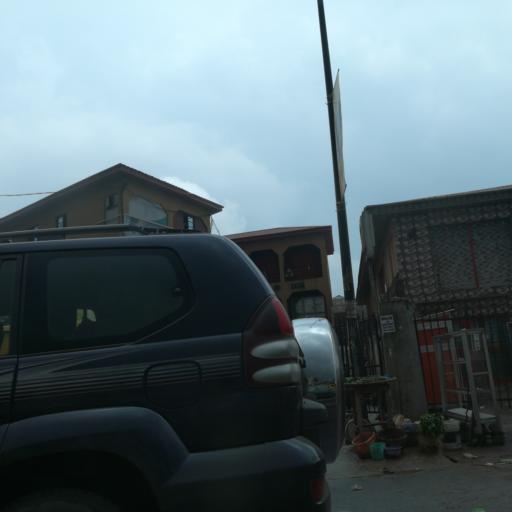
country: NG
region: Lagos
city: Agege
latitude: 6.5995
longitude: 3.2929
